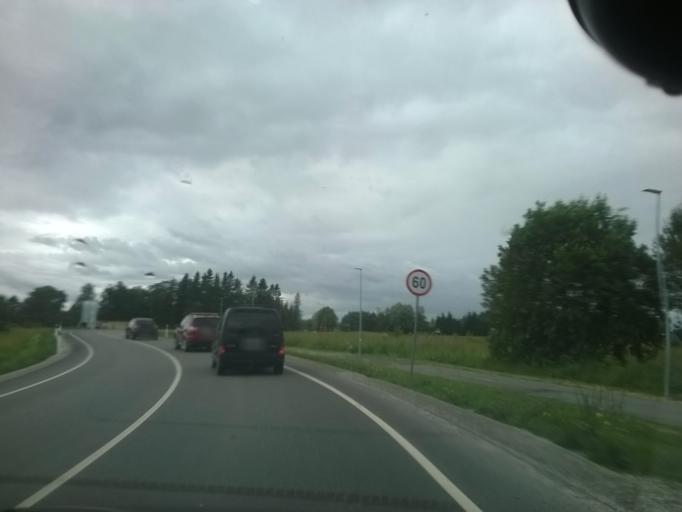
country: EE
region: Harju
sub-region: Rae vald
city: Jueri
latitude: 59.3741
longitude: 24.8614
